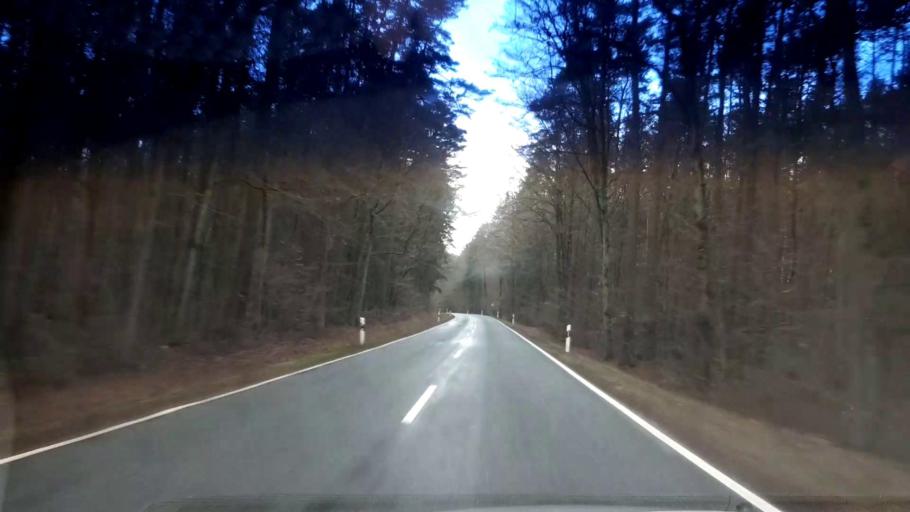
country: DE
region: Bavaria
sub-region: Upper Franconia
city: Lauter
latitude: 49.9650
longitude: 10.7616
